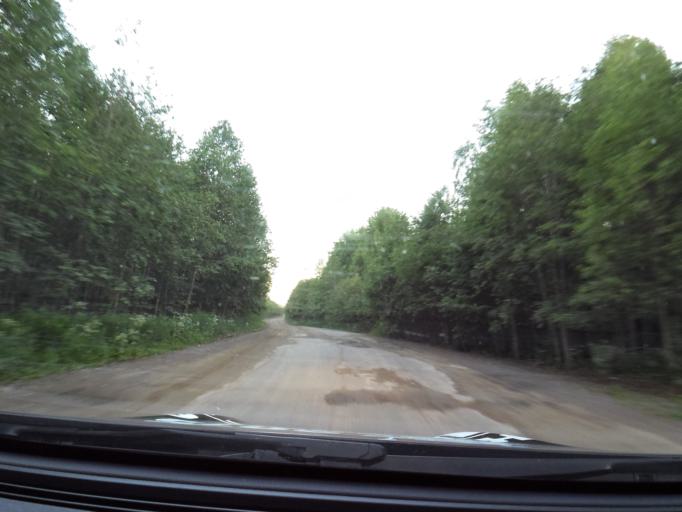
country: RU
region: Leningrad
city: Voznesen'ye
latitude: 60.9521
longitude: 35.4695
